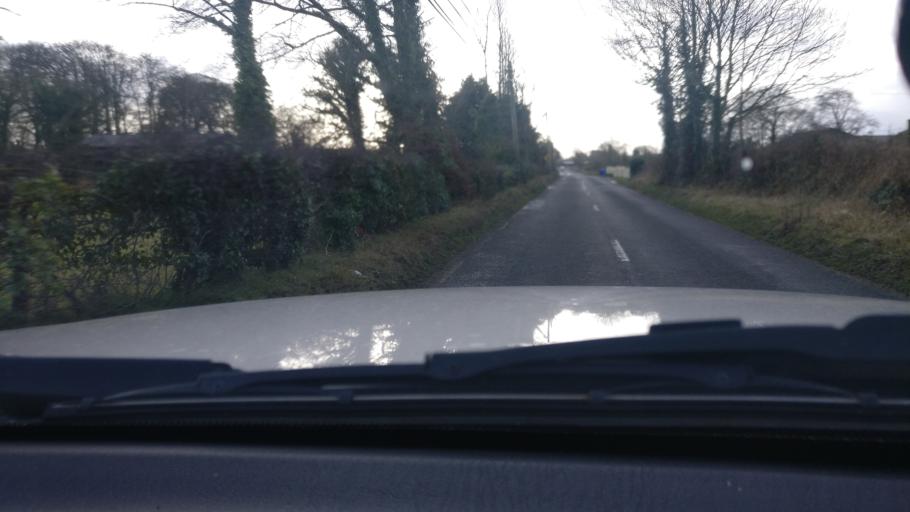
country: IE
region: Connaught
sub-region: County Galway
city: Ballinasloe
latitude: 53.2483
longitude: -8.2644
